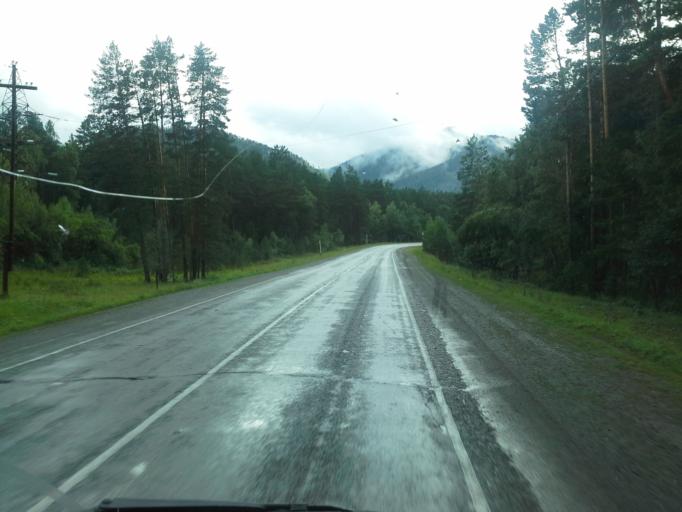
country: RU
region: Altay
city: Elekmonar
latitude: 51.5703
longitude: 85.8969
